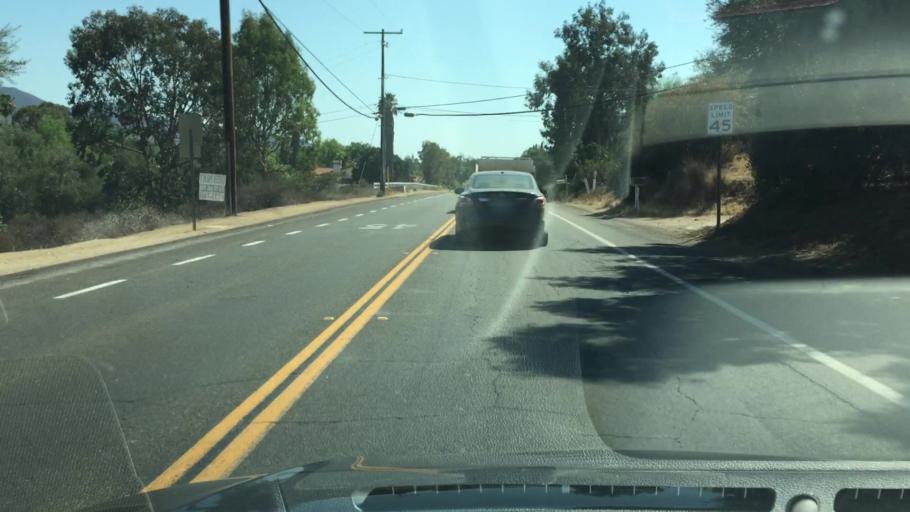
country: US
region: California
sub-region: San Diego County
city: Jamul
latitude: 32.7285
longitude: -116.8652
